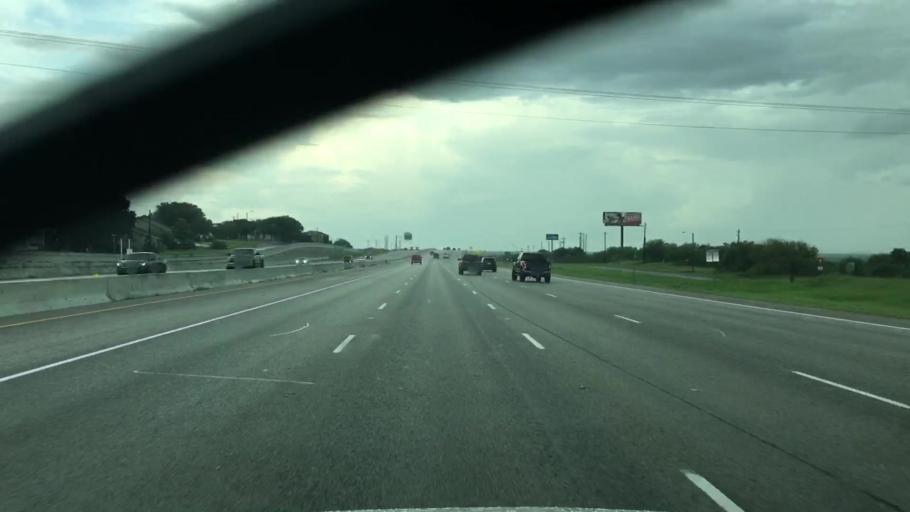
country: US
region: Texas
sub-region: San Patricio County
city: Odem
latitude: 27.8691
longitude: -97.6228
